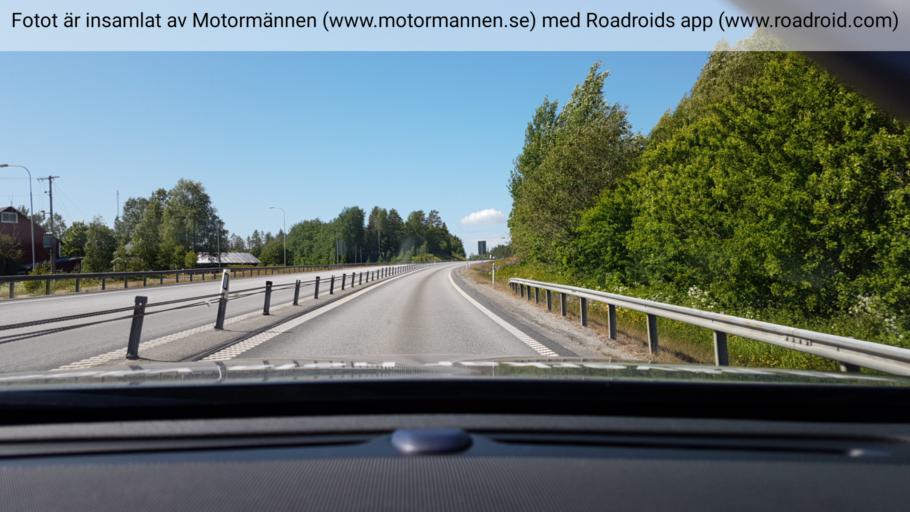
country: SE
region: Vaesterbotten
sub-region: Umea Kommun
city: Roback
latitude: 63.7423
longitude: 20.1277
